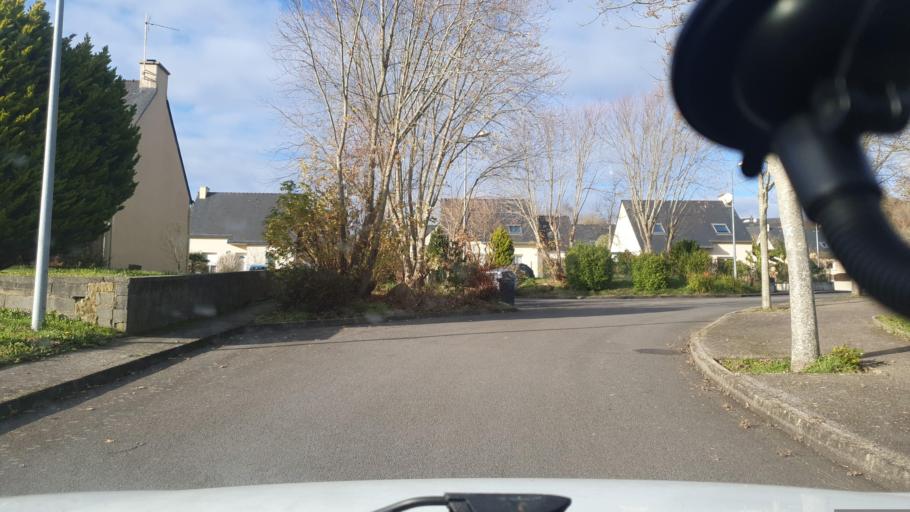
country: FR
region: Brittany
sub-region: Departement du Finistere
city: Briec
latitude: 48.1040
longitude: -3.9913
